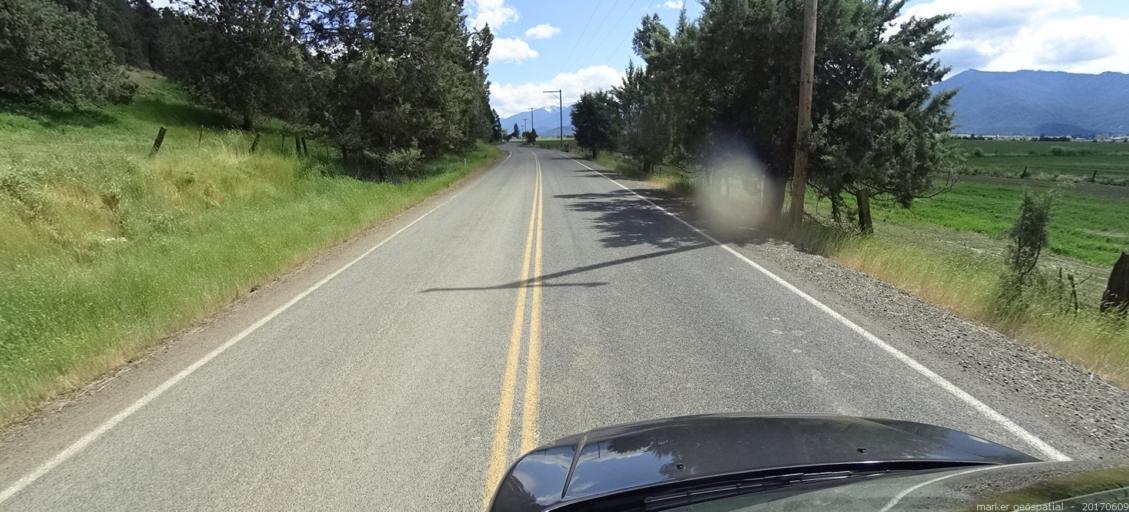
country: US
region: California
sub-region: Siskiyou County
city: Yreka
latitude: 41.5145
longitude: -122.8397
